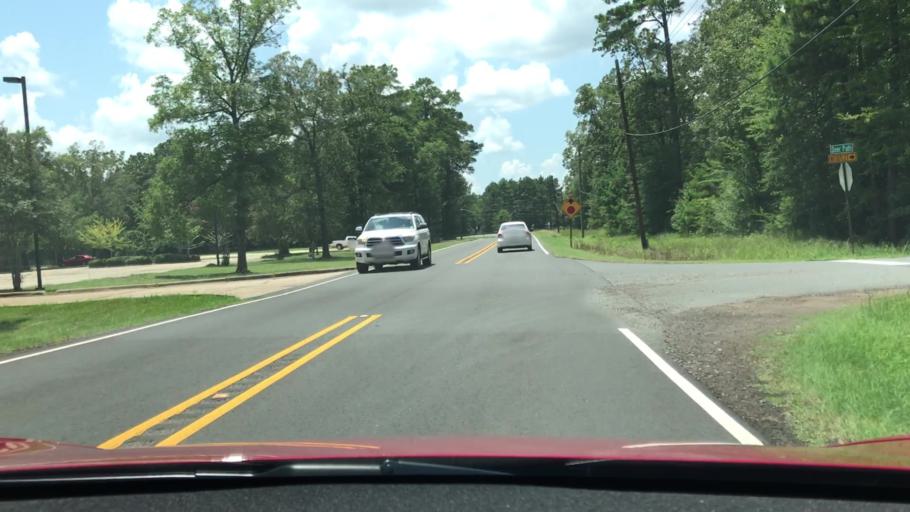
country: US
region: Louisiana
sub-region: Bossier Parish
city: Bossier City
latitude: 32.3649
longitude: -93.6897
